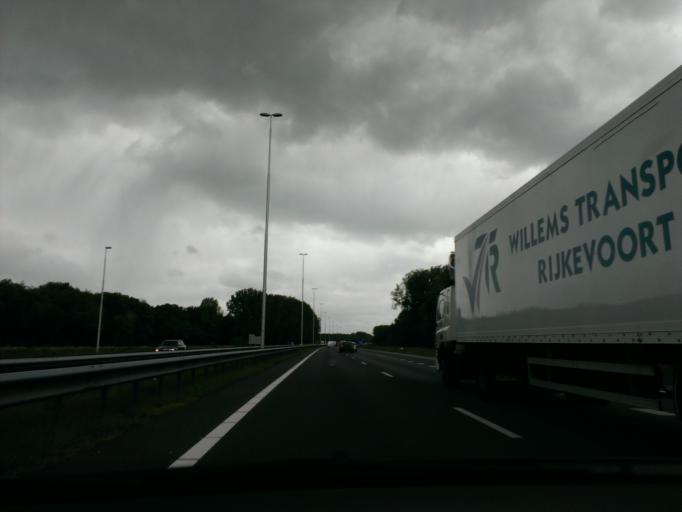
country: NL
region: Gelderland
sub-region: Gemeente Nijmegen
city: Lindenholt
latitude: 51.8030
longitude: 5.7900
